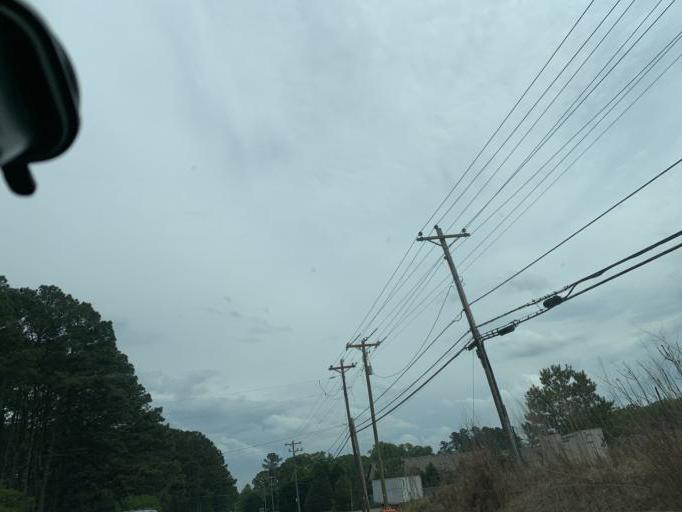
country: US
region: Georgia
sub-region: Forsyth County
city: Cumming
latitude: 34.1816
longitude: -84.0945
